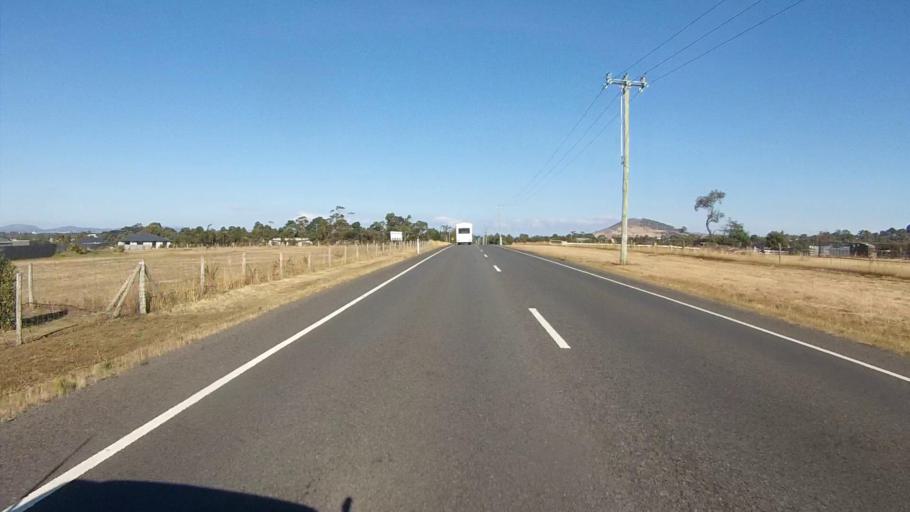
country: AU
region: Tasmania
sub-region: Clarence
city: Cambridge
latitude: -42.8409
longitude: 147.4695
